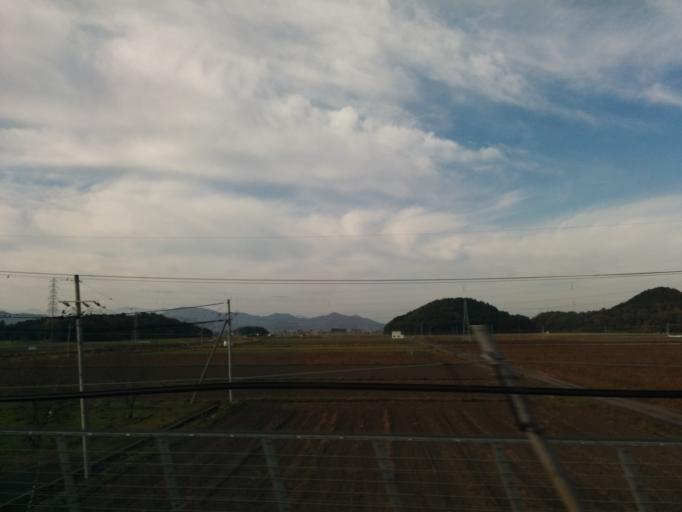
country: JP
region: Shiga Prefecture
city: Omihachiman
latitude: 35.1225
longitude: 136.1386
